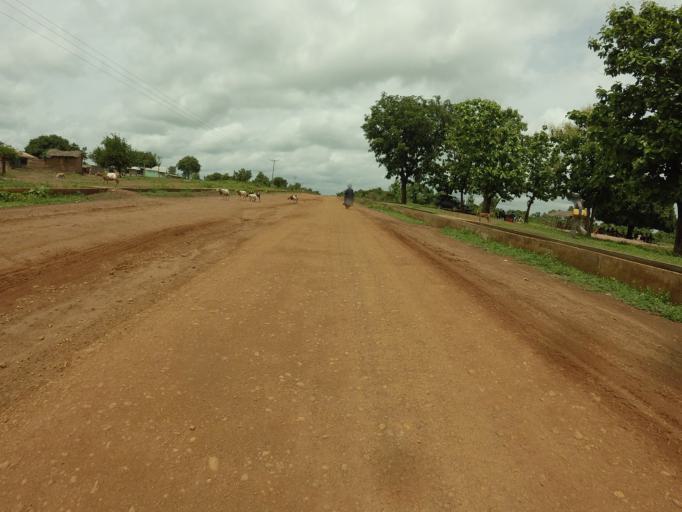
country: GH
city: Kpandae
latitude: 8.4528
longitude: 0.3469
